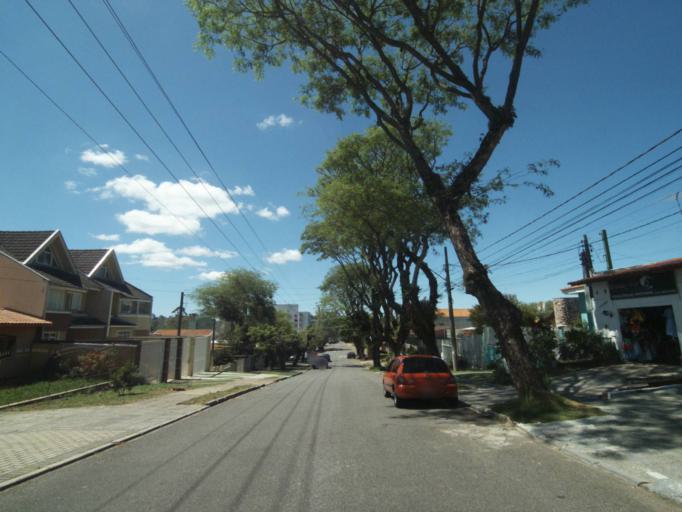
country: BR
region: Parana
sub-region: Curitiba
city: Curitiba
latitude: -25.3908
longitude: -49.2423
